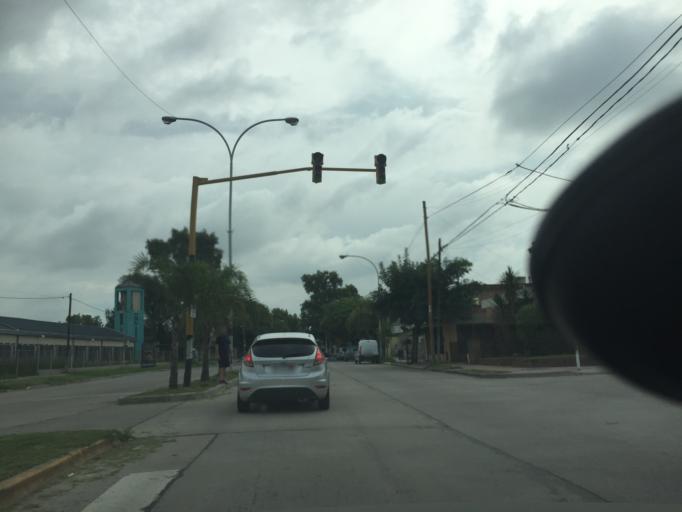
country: AR
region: Cordoba
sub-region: Departamento de Capital
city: Cordoba
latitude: -31.4507
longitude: -64.2010
